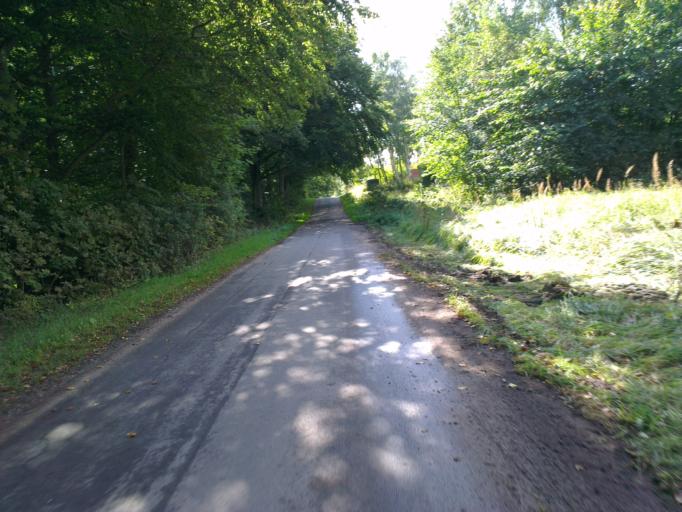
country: DK
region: Capital Region
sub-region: Frederikssund Kommune
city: Jaegerspris
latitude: 55.8725
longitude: 11.9848
